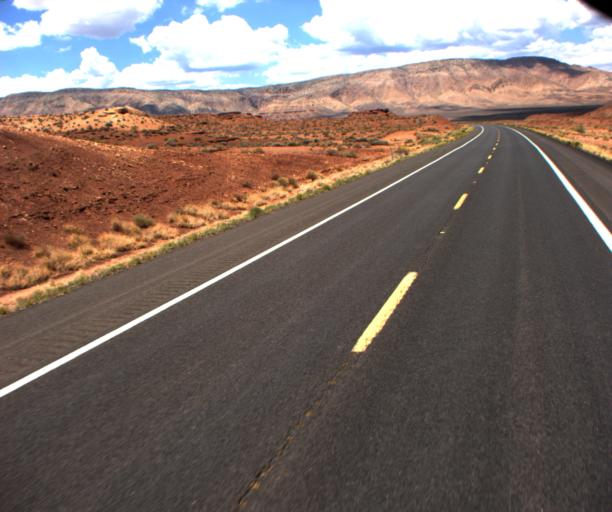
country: US
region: Arizona
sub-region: Coconino County
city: Tuba City
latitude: 35.8721
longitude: -111.5000
